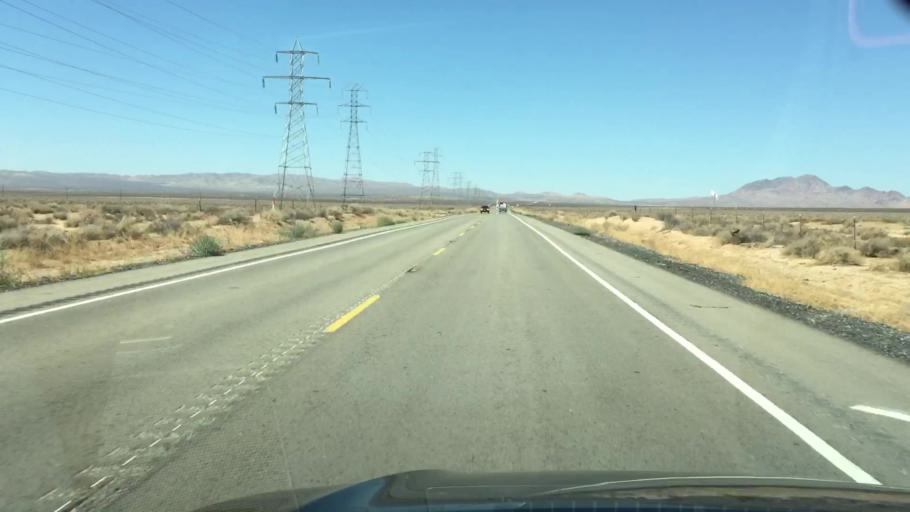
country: US
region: California
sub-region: Kern County
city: Boron
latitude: 35.1985
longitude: -117.5991
